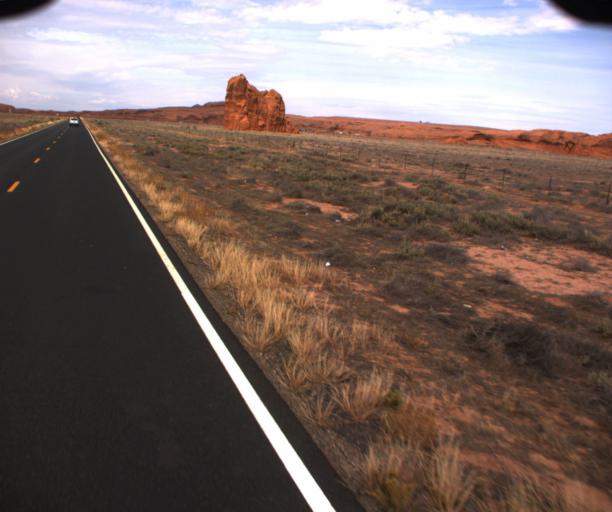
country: US
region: Arizona
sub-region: Apache County
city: Many Farms
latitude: 36.7437
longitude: -109.6388
